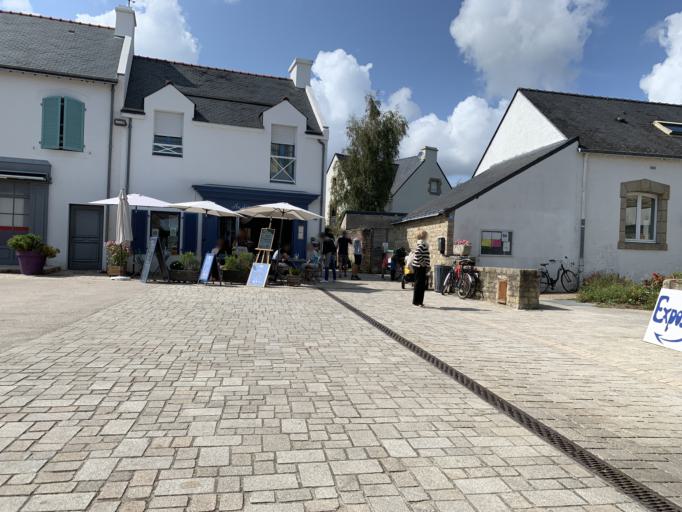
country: FR
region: Brittany
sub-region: Departement du Morbihan
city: Arradon
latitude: 47.5968
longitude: -2.8457
